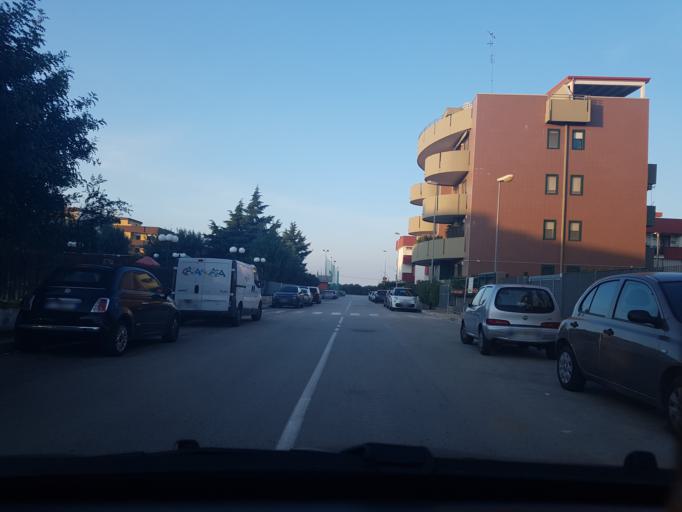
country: IT
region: Apulia
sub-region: Provincia di Bari
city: Bitritto
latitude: 41.0482
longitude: 16.8252
